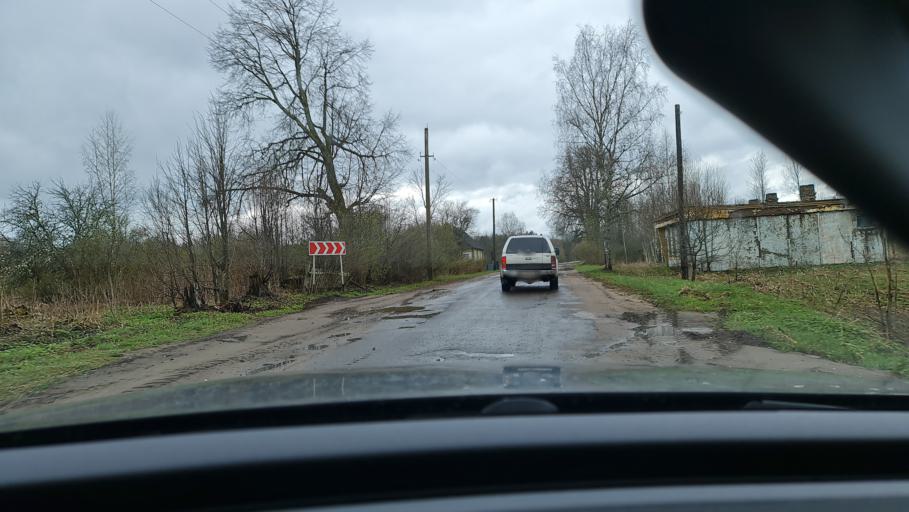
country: RU
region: Novgorod
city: Marevo
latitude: 57.2398
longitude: 32.0411
